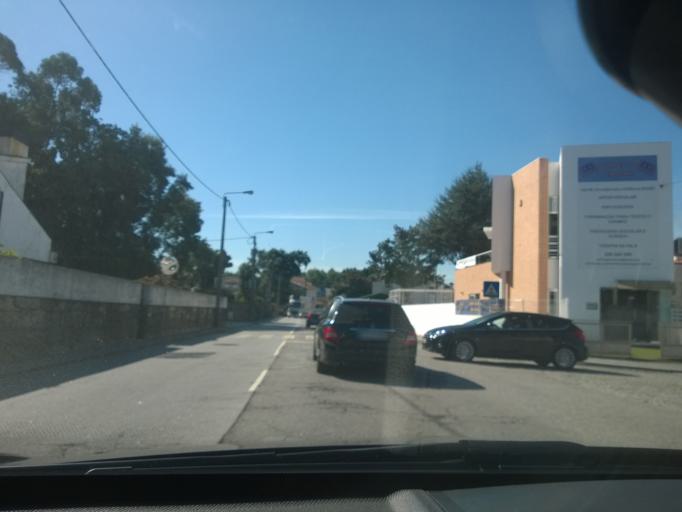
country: PT
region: Porto
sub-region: Maia
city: Gemunde
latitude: 41.2510
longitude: -8.6588
